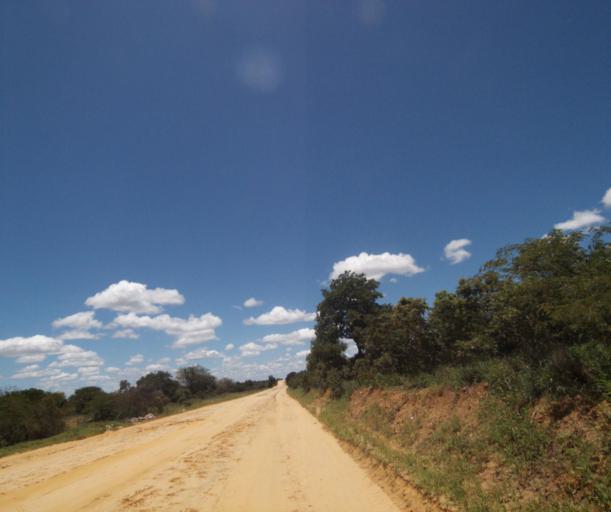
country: BR
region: Bahia
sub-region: Carinhanha
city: Carinhanha
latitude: -14.2849
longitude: -43.7872
